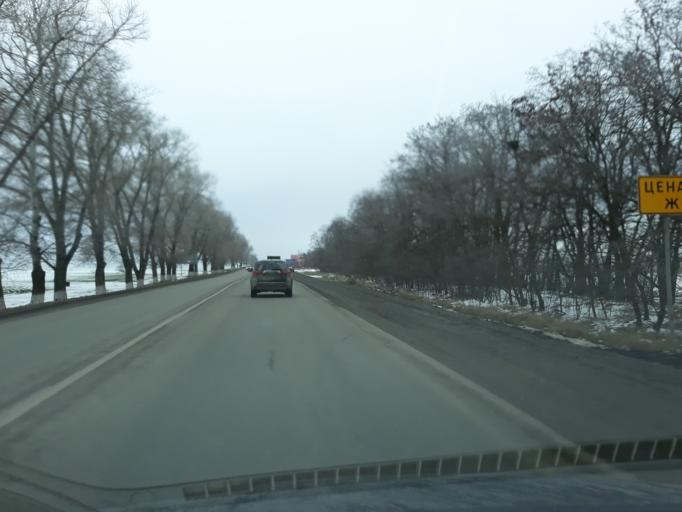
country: RU
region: Rostov
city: Primorka
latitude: 47.3013
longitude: 38.9854
